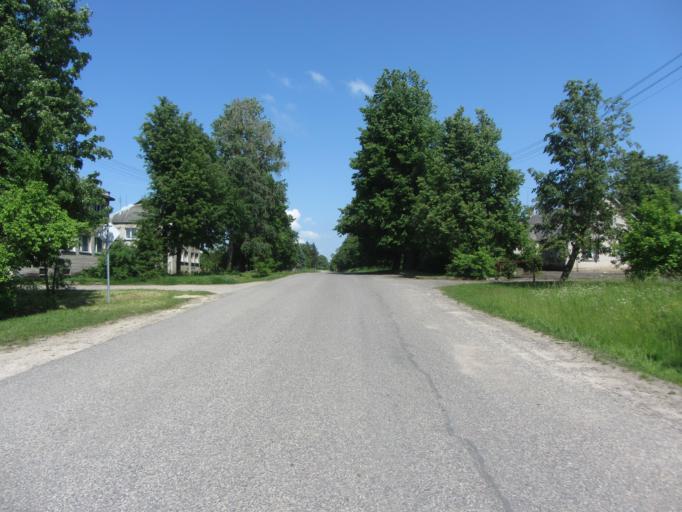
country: LT
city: Kaisiadorys
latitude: 54.8503
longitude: 24.3411
